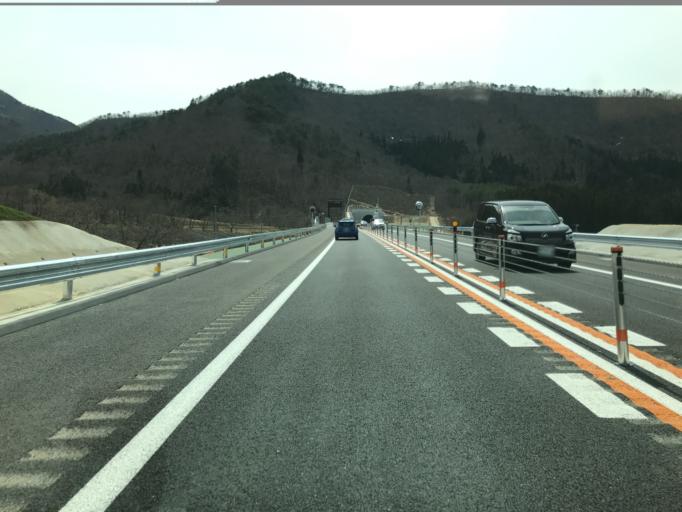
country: JP
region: Yamagata
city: Kaminoyama
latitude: 38.0920
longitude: 140.2094
